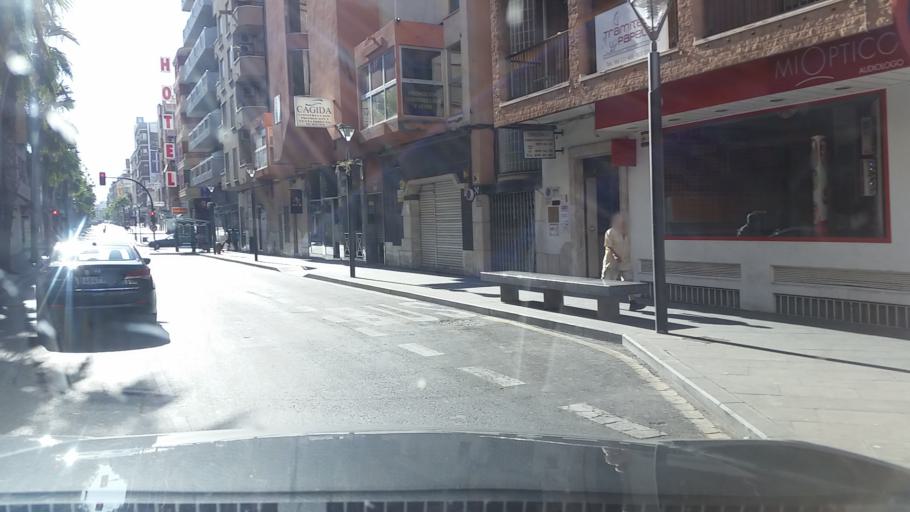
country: ES
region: Valencia
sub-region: Provincia de Alicante
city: Torrevieja
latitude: 37.9773
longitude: -0.6804
